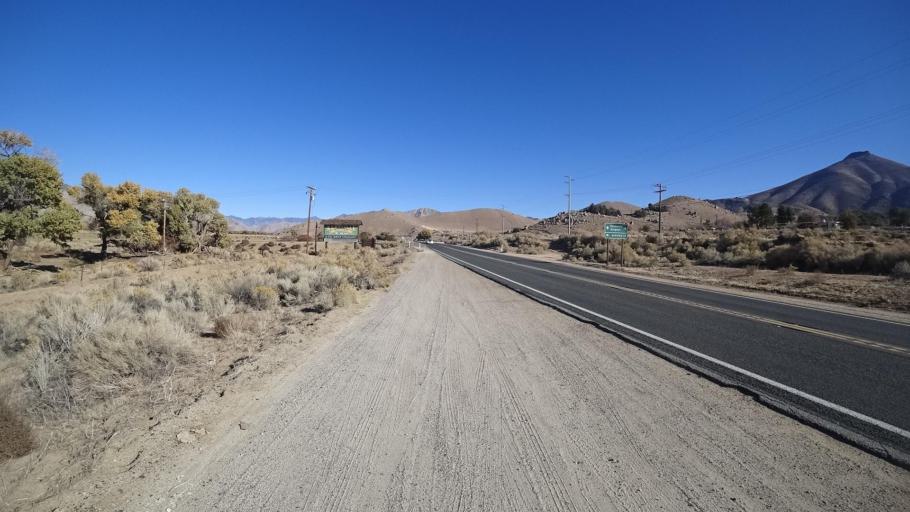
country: US
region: California
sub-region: Kern County
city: Weldon
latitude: 35.6571
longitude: -118.3243
